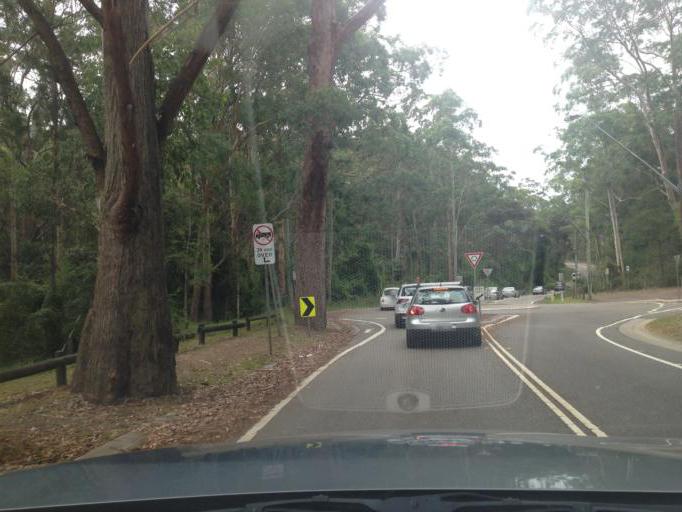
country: AU
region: New South Wales
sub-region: Ku-ring-gai
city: Lindfield
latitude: -33.7865
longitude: 151.1549
